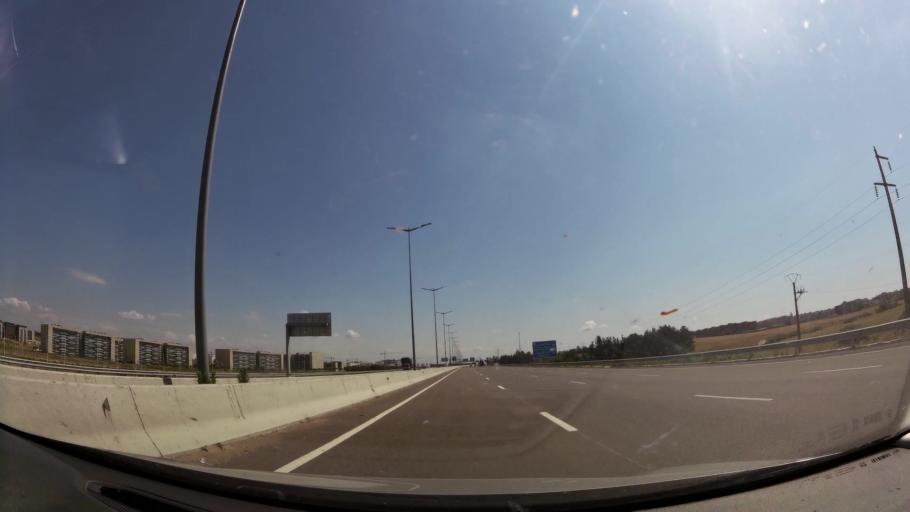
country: MA
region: Rabat-Sale-Zemmour-Zaer
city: Sale
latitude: 33.9966
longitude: -6.7225
